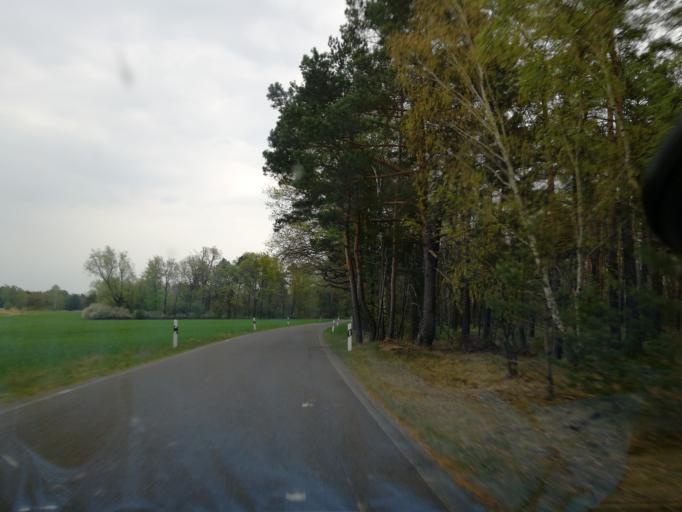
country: DE
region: Brandenburg
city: Calau
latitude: 51.7888
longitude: 13.8860
